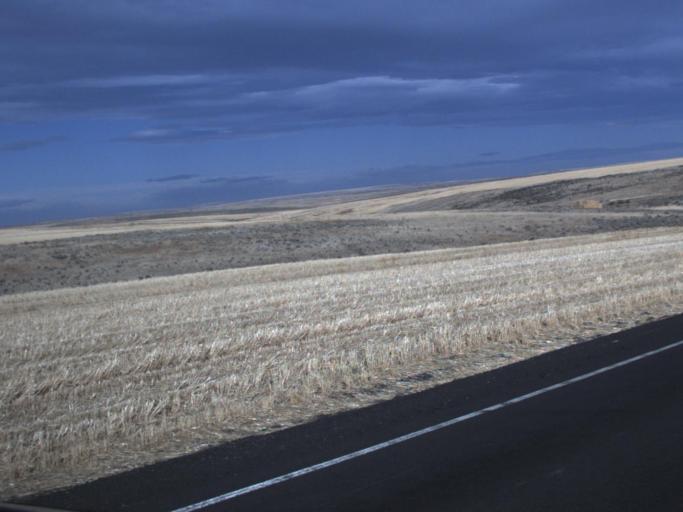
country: US
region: Washington
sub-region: Adams County
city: Ritzville
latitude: 47.2879
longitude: -118.6902
